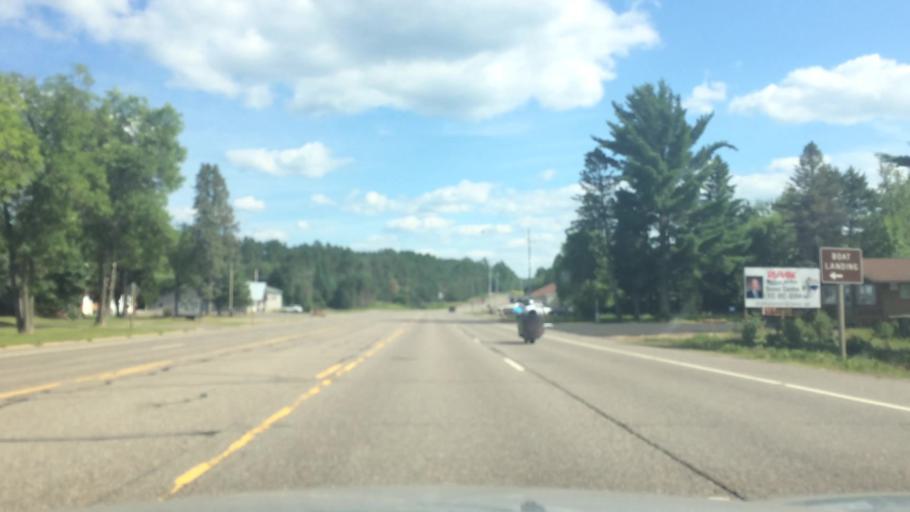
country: US
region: Wisconsin
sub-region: Vilas County
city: Lac du Flambeau
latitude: 45.8072
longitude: -89.7247
